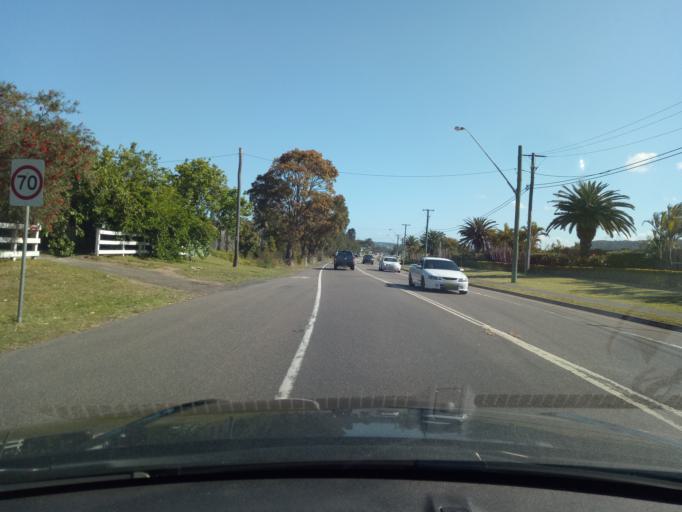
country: AU
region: New South Wales
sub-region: Gosford Shire
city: Forresters Beach
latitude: -33.4026
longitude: 151.4678
